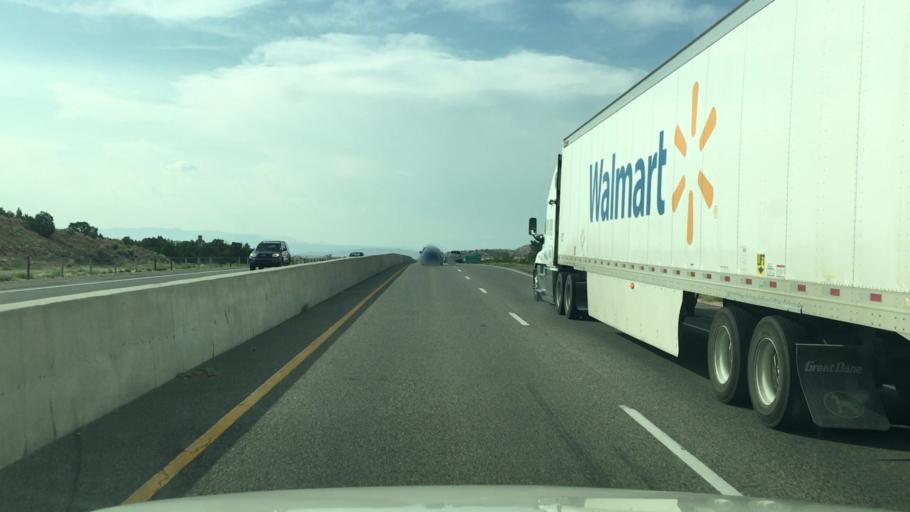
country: US
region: New Mexico
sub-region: Santa Fe County
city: Nambe
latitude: 35.8111
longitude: -105.9677
